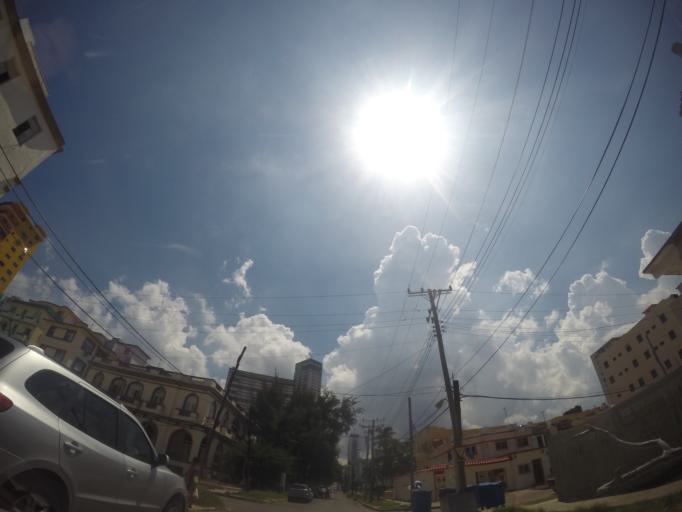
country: CU
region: La Habana
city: Havana
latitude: 23.1447
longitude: -82.3865
